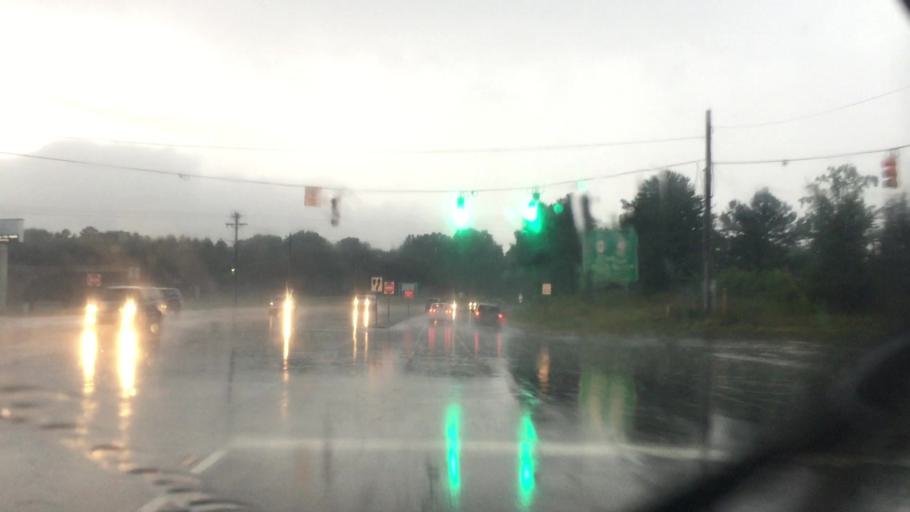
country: US
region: North Carolina
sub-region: Rowan County
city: Salisbury
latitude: 35.6480
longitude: -80.4942
